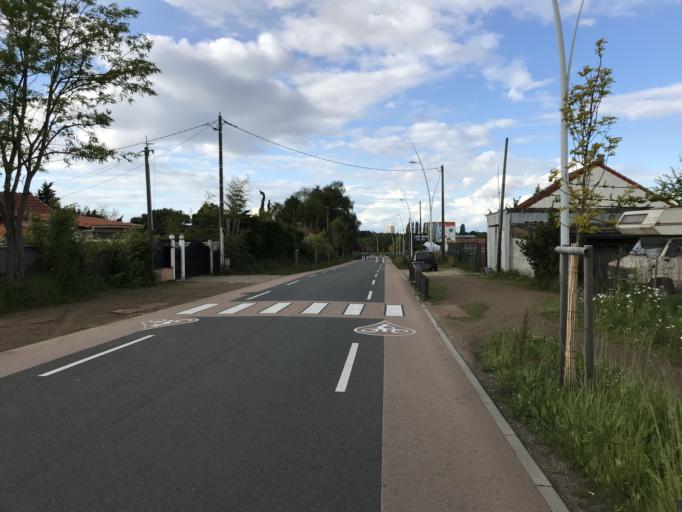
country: FR
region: Ile-de-France
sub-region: Departement de l'Essonne
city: Wissous
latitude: 48.7356
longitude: 2.3362
